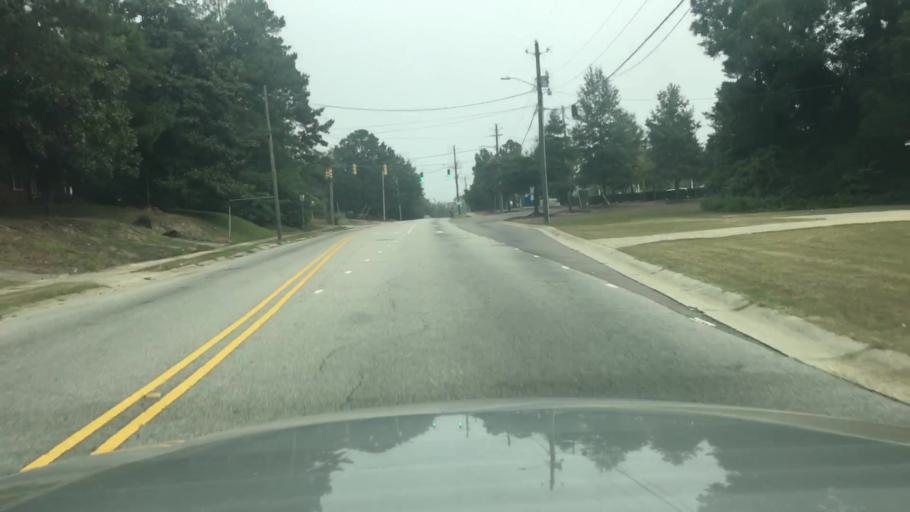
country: US
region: North Carolina
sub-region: Cumberland County
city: Fayetteville
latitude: 35.0697
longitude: -78.8838
